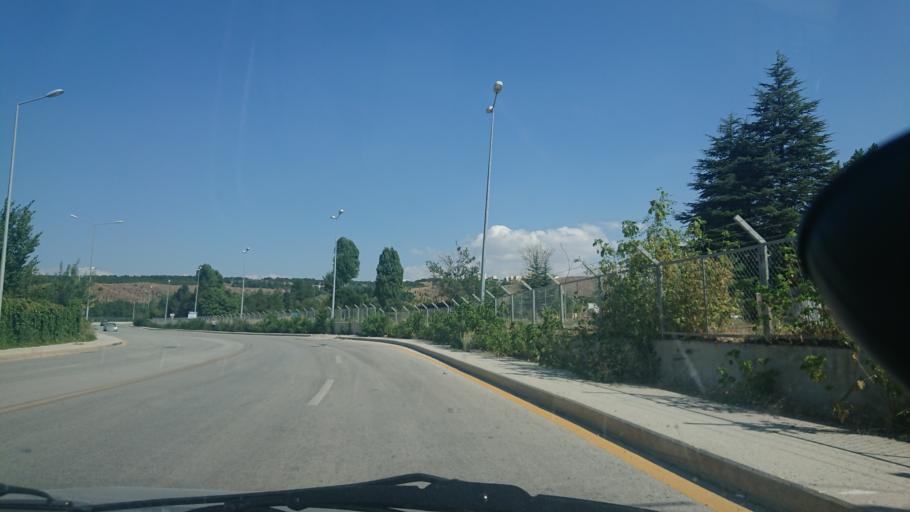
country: TR
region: Ankara
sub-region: Goelbasi
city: Golbasi
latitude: 39.8067
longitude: 32.8203
